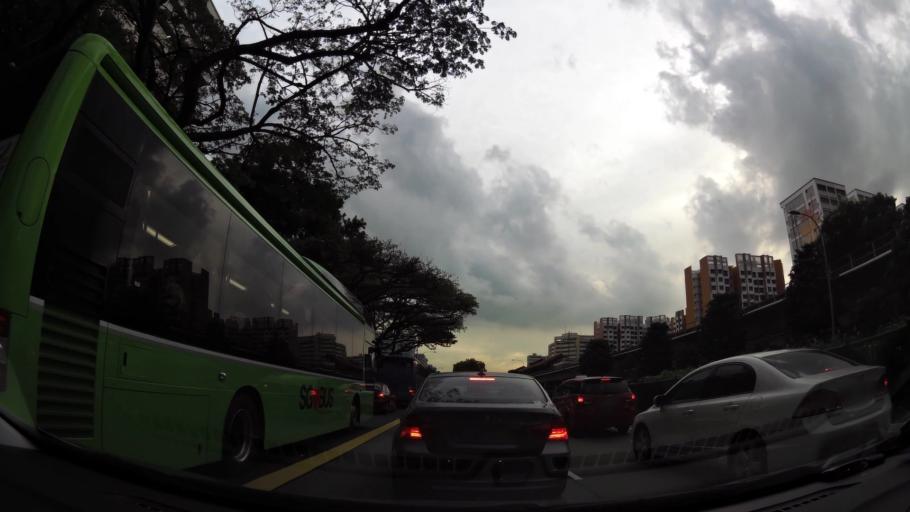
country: MY
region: Johor
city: Kampung Pasir Gudang Baru
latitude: 1.4190
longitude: 103.8342
